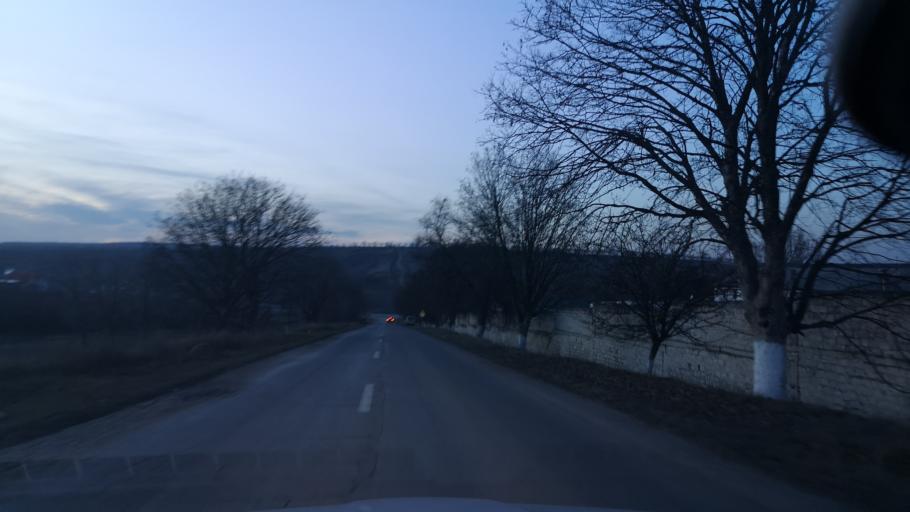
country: MD
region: Orhei
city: Orhei
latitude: 47.3084
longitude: 28.9357
